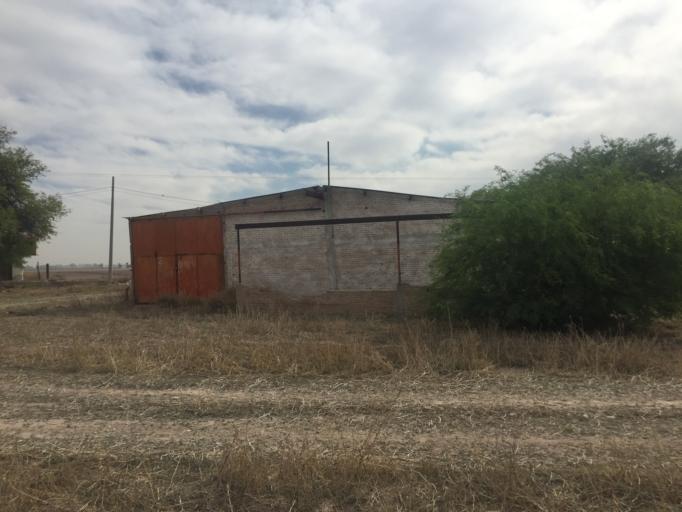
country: MX
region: Durango
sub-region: Gomez Palacio
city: El Vergel
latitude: 25.6635
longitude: -103.5221
